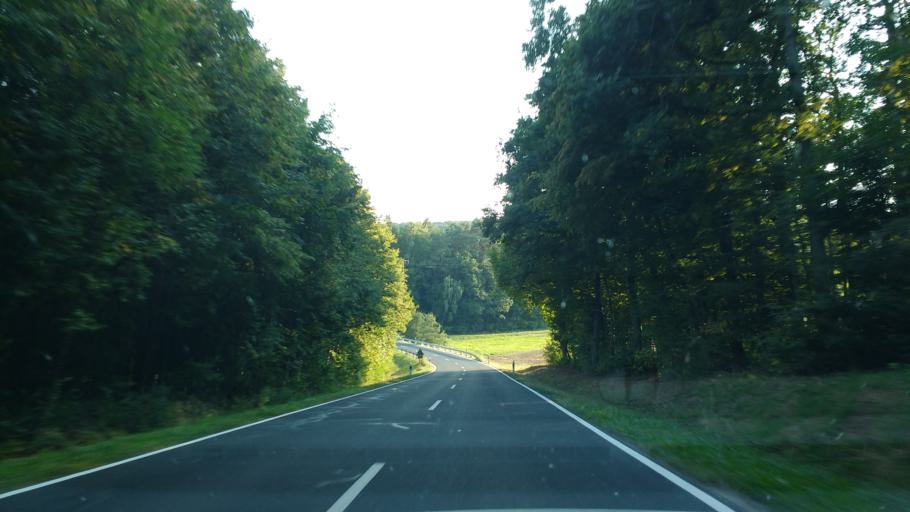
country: DE
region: Bavaria
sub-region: Regierungsbezirk Unterfranken
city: Elfershausen
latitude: 50.1669
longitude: 9.9581
